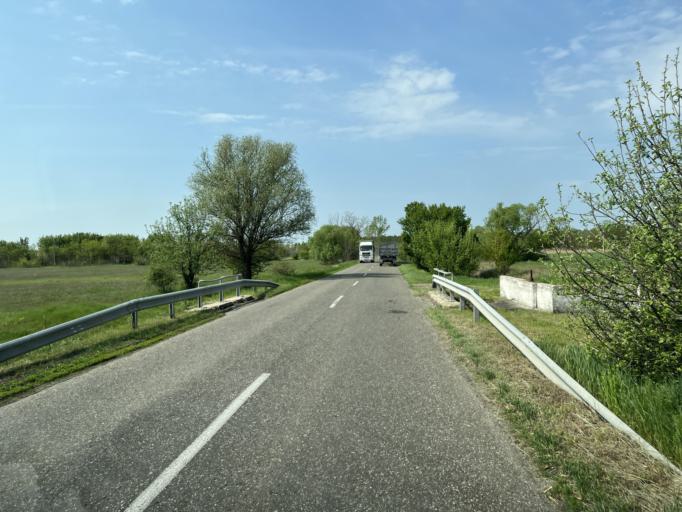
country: HU
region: Pest
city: Tortel
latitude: 47.0927
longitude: 19.8908
